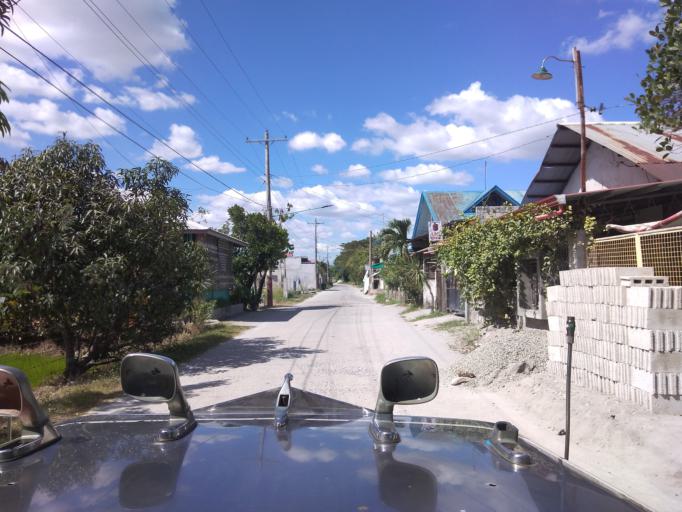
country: PH
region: Central Luzon
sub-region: Province of Pampanga
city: Bacolor
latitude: 15.0119
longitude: 120.6435
